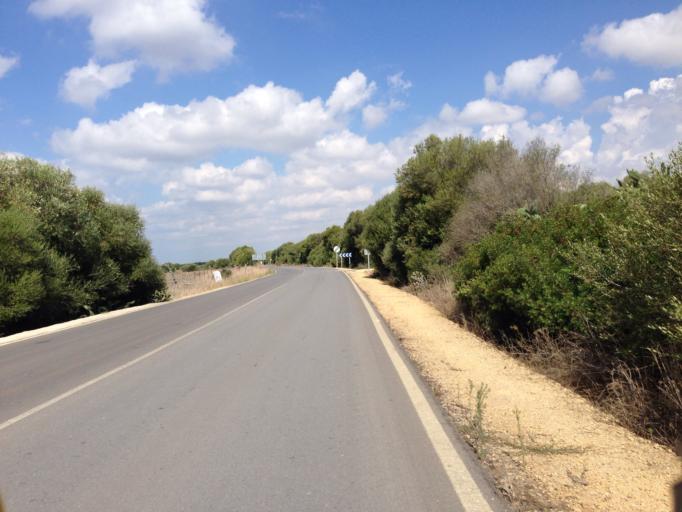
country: ES
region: Andalusia
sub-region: Provincia de Cadiz
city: Vejer de la Frontera
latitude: 36.2158
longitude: -6.0367
